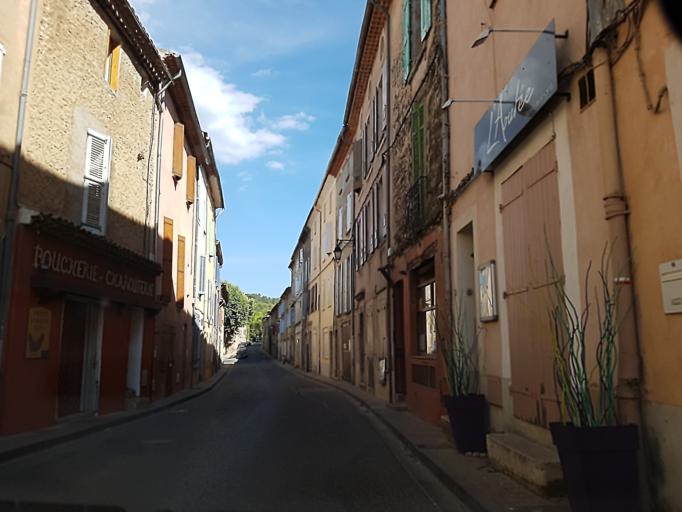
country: FR
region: Provence-Alpes-Cote d'Azur
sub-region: Departement du Var
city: Bras
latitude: 43.4720
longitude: 5.9539
